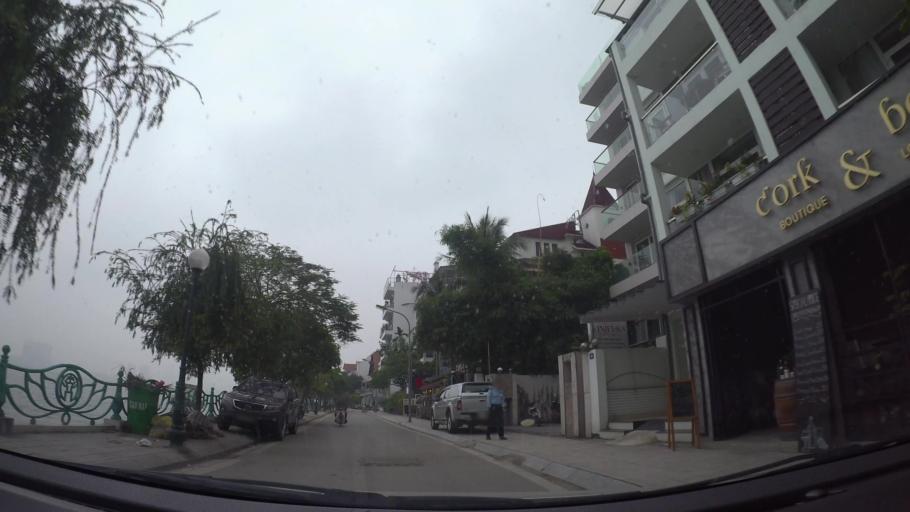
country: VN
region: Ha Noi
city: Tay Ho
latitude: 21.0611
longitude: 105.8280
